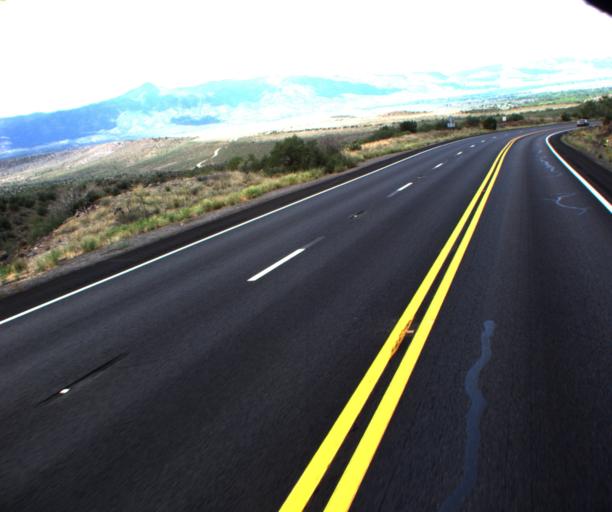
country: US
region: Arizona
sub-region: Yavapai County
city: Camp Verde
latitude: 34.5086
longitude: -111.7389
